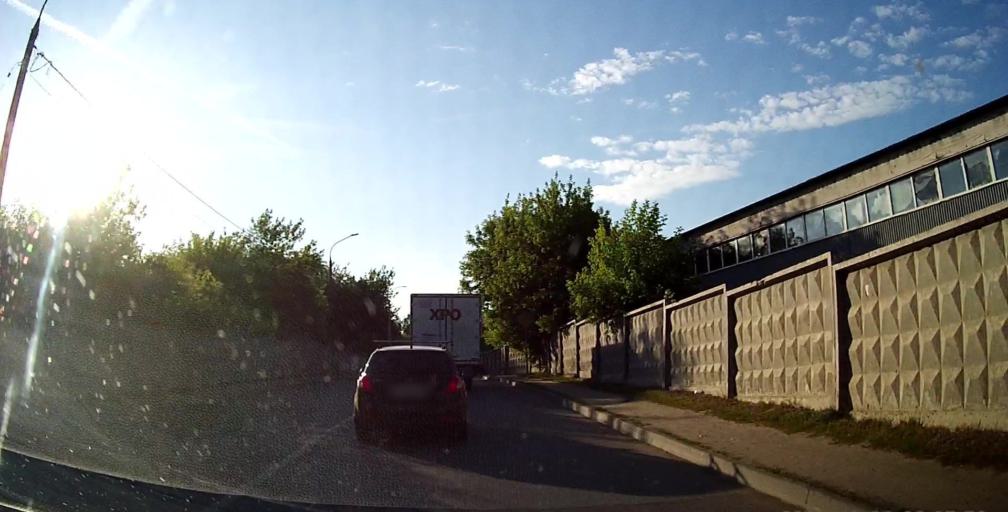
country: RU
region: Moskovskaya
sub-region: Podol'skiy Rayon
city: Podol'sk
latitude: 55.4378
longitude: 37.5832
